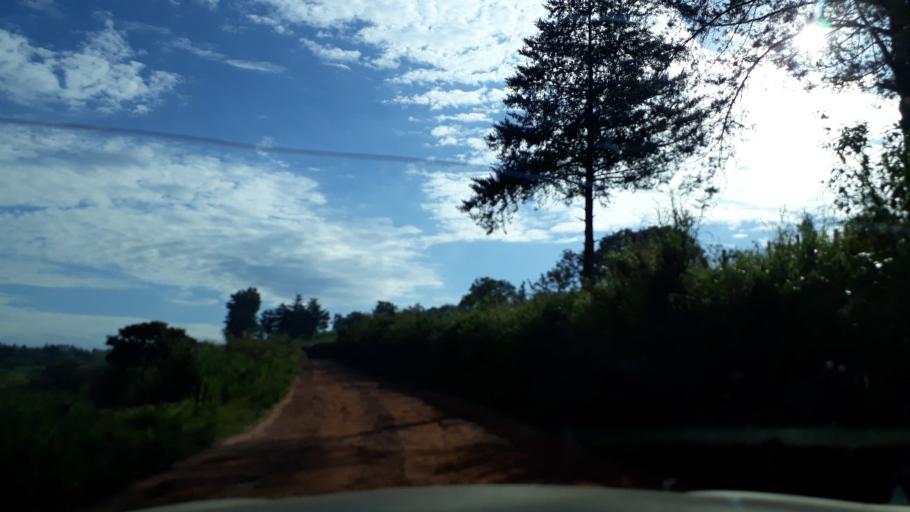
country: UG
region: Northern Region
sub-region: Zombo District
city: Paidha
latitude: 2.2621
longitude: 30.9412
